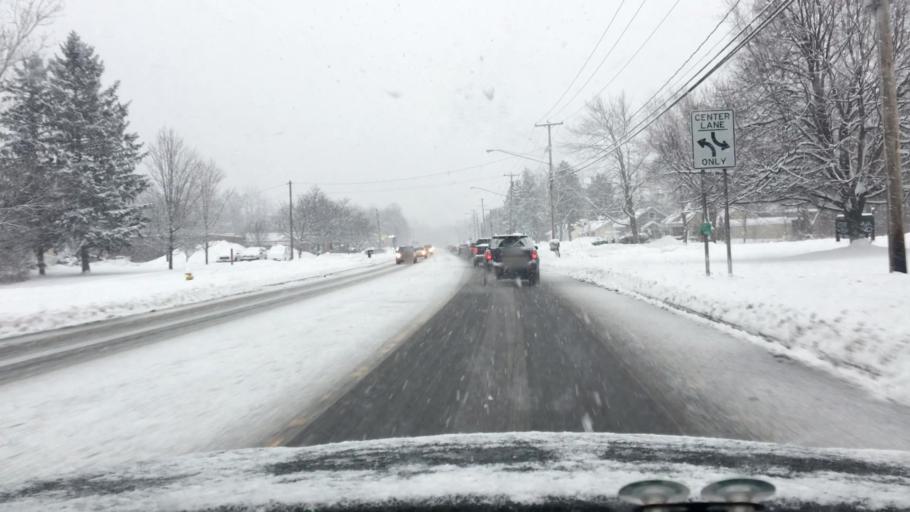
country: US
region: New York
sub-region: Erie County
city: Orchard Park
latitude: 42.7858
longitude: -78.7487
